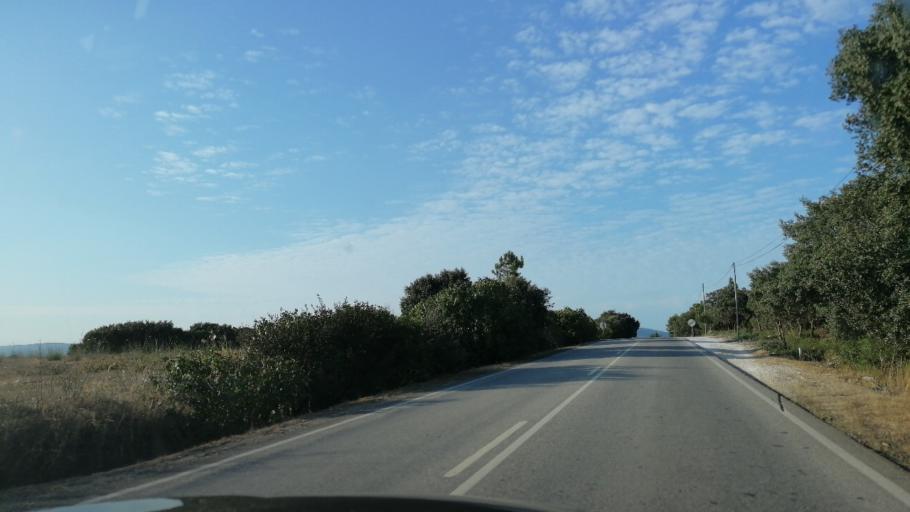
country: PT
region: Santarem
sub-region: Alcanena
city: Alcanena
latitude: 39.4234
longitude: -8.6350
